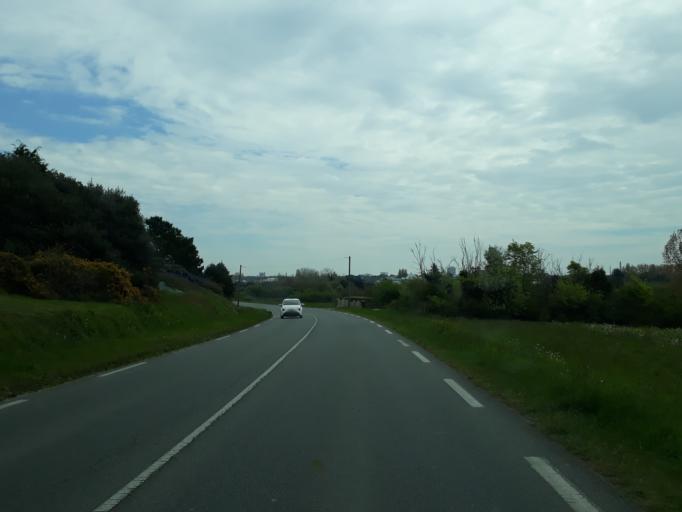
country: FR
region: Pays de la Loire
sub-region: Departement de la Loire-Atlantique
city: Le Pouliguen
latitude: 47.2965
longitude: -2.4041
